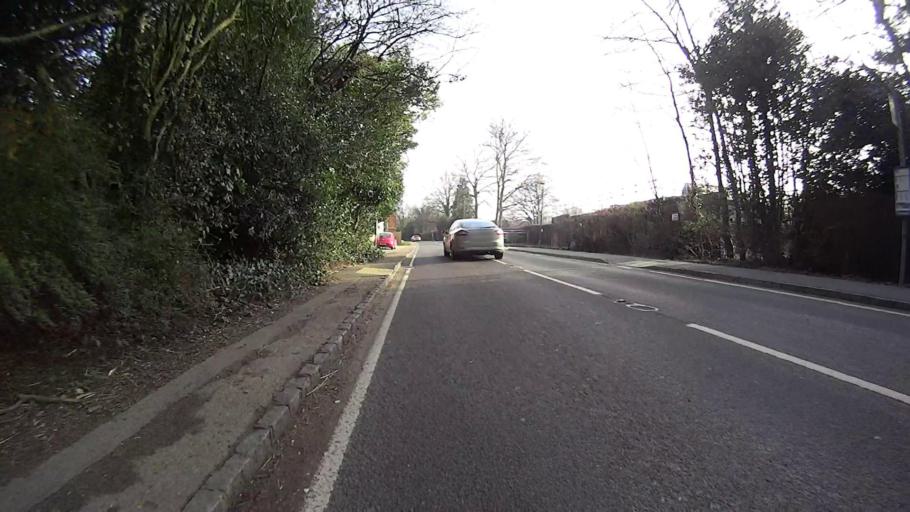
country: GB
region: England
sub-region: West Sussex
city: Crawley Down
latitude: 51.1263
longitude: -0.0894
